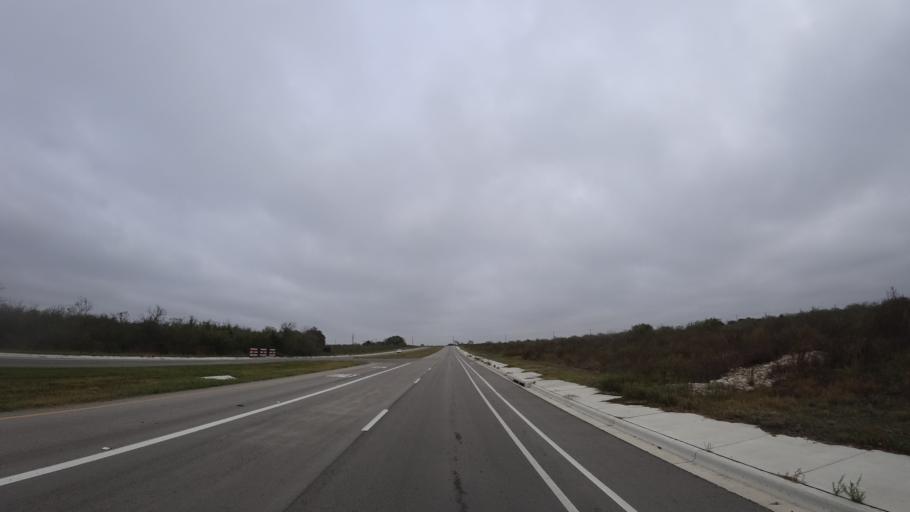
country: US
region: Texas
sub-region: Travis County
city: Pflugerville
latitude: 30.4112
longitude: -97.6123
